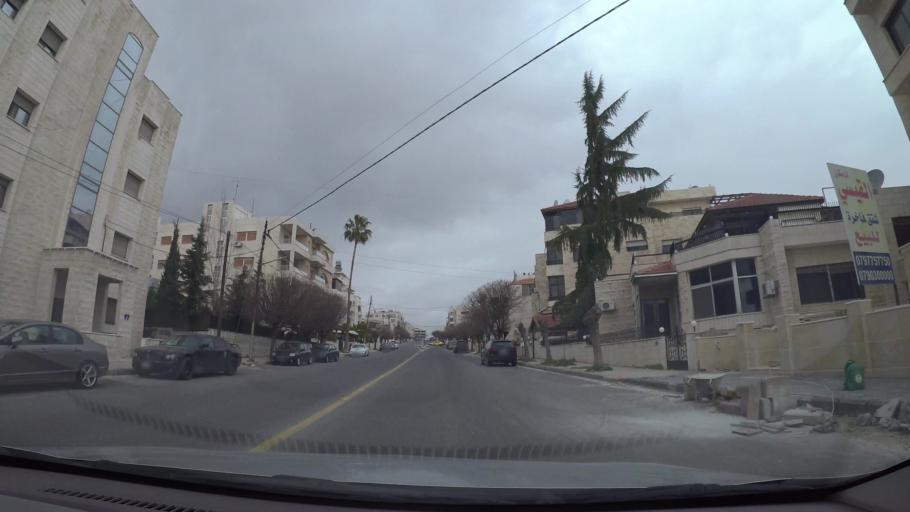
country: JO
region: Amman
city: Wadi as Sir
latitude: 31.9719
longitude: 35.8521
